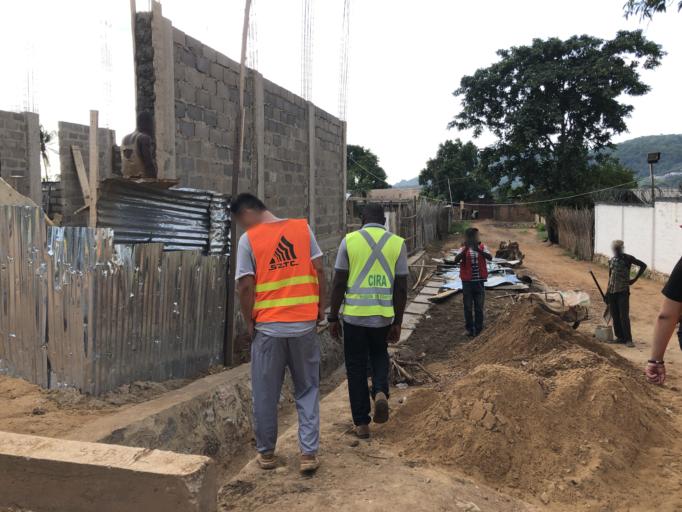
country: CF
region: Bangui
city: Bangui
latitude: 4.3515
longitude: 18.5970
